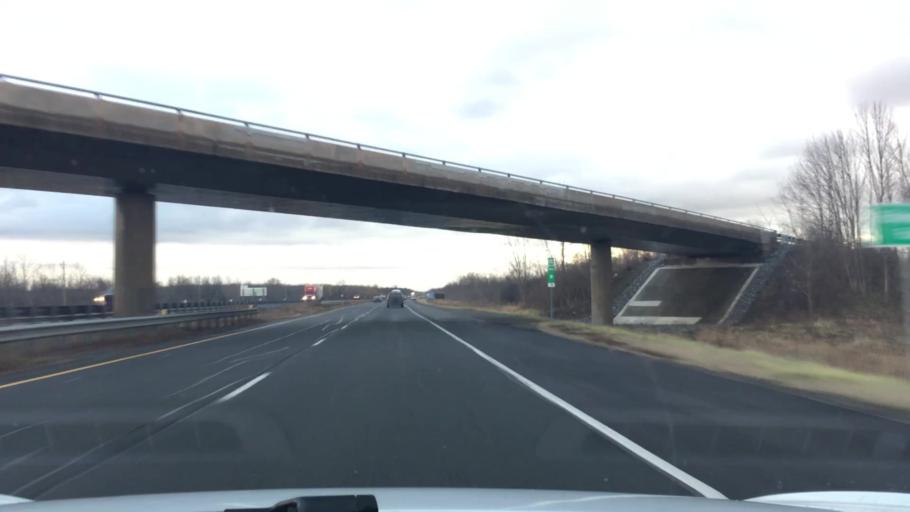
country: US
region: New York
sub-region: Erie County
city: Grandyle Village
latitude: 42.9516
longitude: -79.0064
